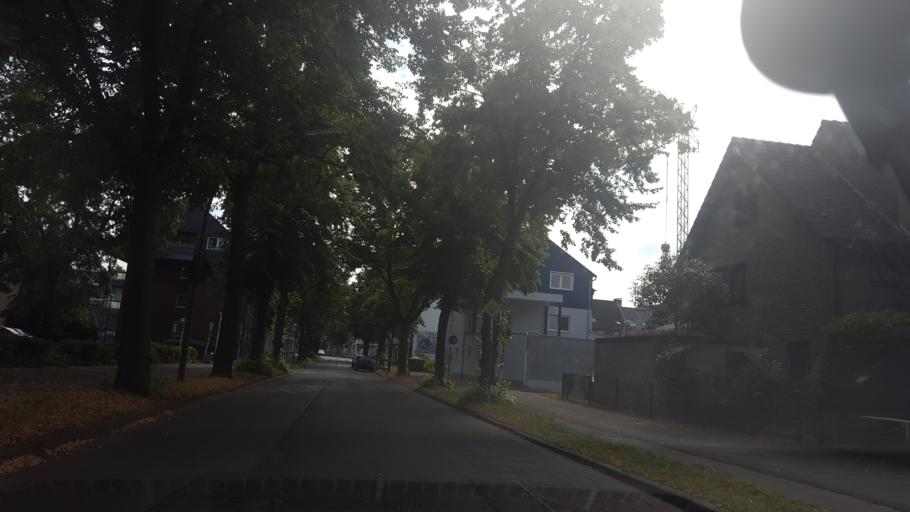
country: DE
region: North Rhine-Westphalia
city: Marl
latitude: 51.6575
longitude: 7.0872
